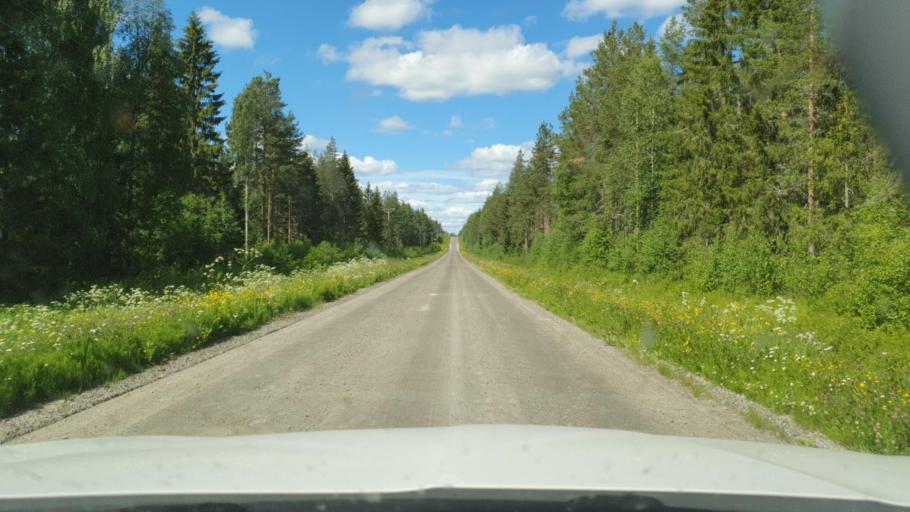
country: SE
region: Vaesterbotten
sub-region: Skelleftea Kommun
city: Backa
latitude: 65.1713
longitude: 21.1084
